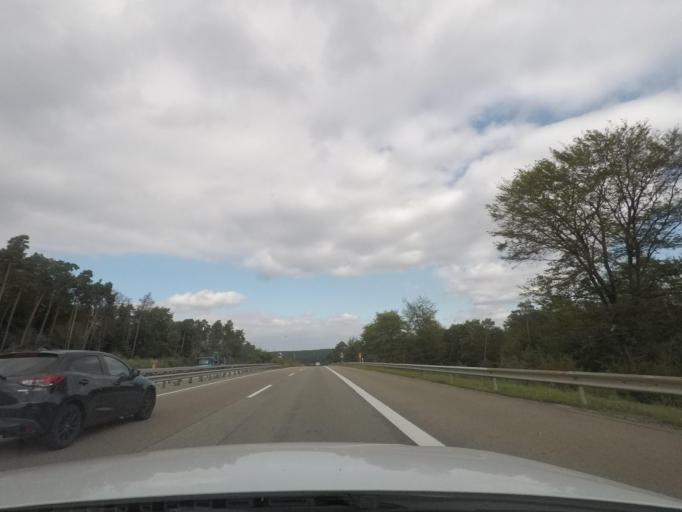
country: DE
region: Rheinland-Pfalz
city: Carlsberg
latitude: 49.5065
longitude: 8.0166
